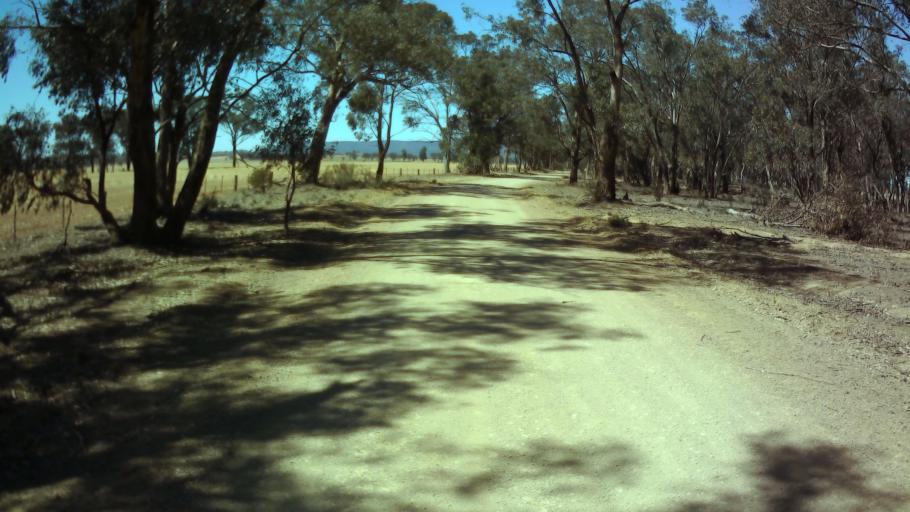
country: AU
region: New South Wales
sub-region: Weddin
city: Grenfell
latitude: -33.8884
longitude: 148.0875
